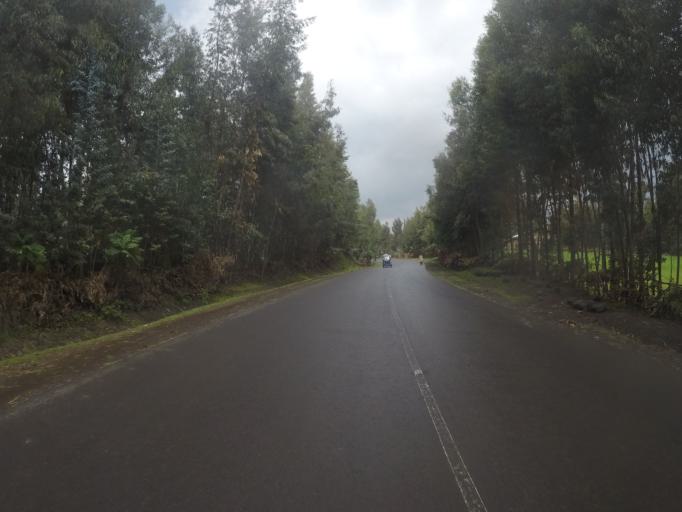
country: ET
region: Amhara
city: Debark'
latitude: 13.1174
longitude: 37.8738
